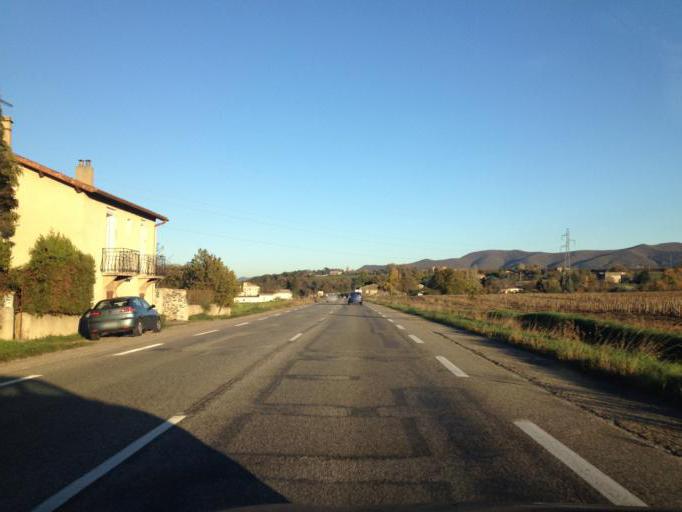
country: FR
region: Rhone-Alpes
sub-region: Departement de l'Ardeche
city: Chomerac
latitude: 44.7093
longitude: 4.6884
